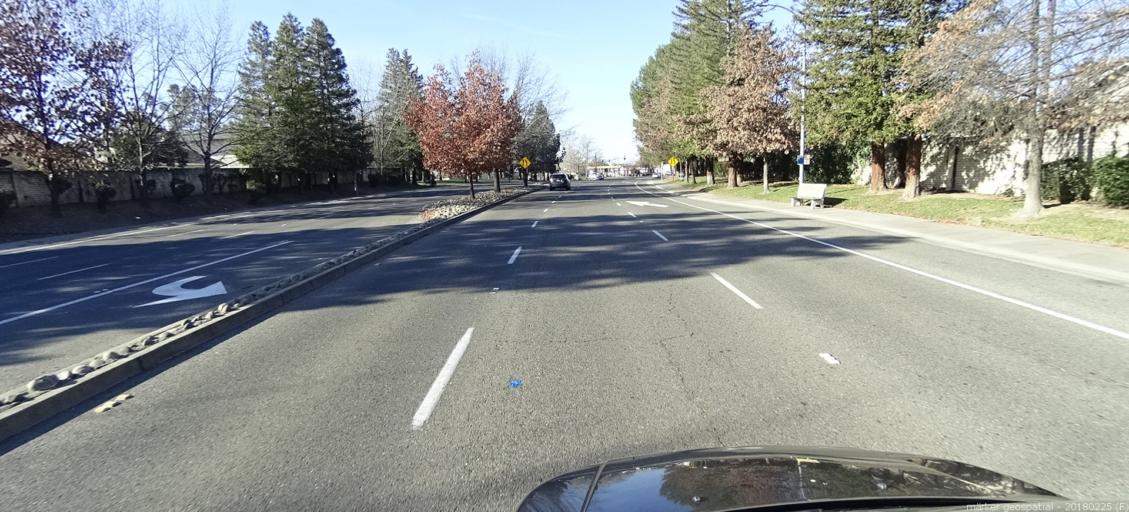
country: US
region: California
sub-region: Sacramento County
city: North Highlands
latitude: 38.7152
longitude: -121.3901
